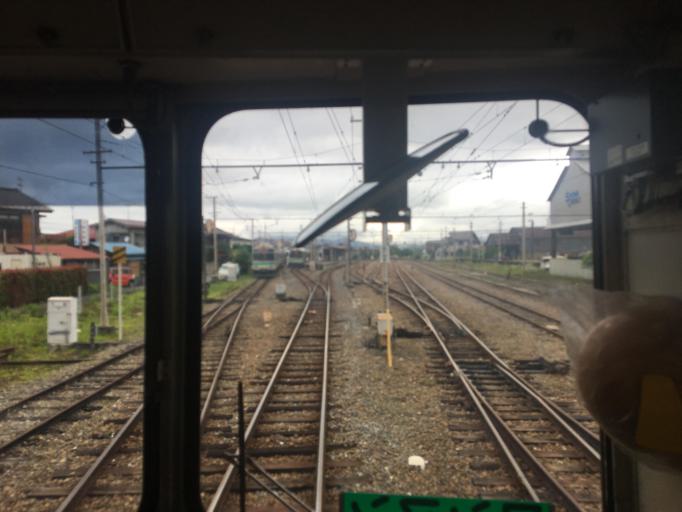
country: JP
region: Saitama
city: Chichibu
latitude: 35.9711
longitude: 139.0677
